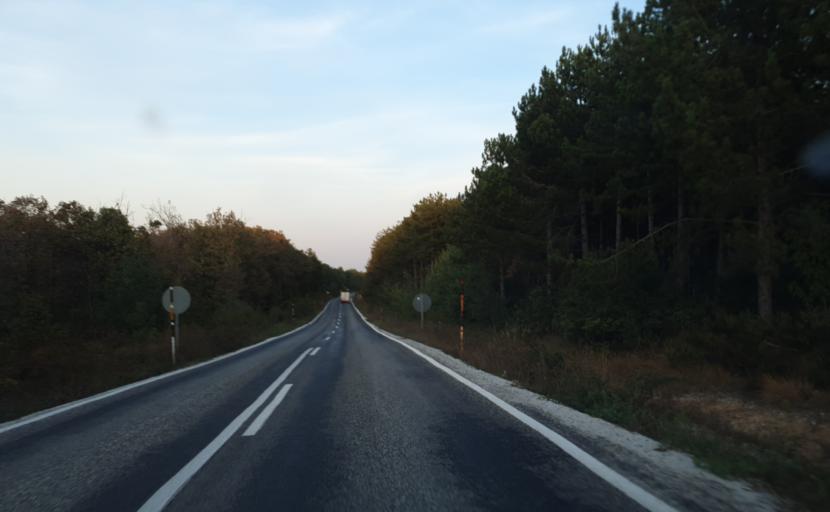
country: TR
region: Kirklareli
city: Igneada
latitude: 41.8620
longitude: 27.8725
